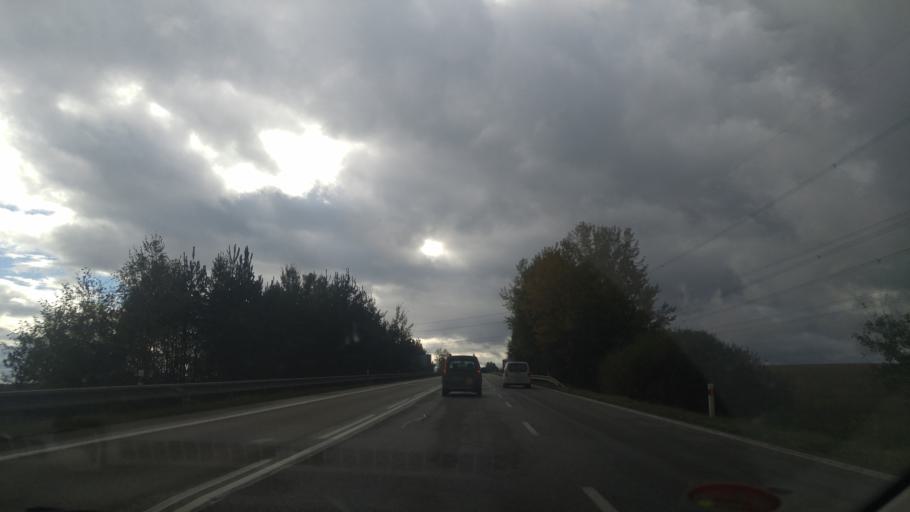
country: CZ
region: Jihocesky
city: Sevetin
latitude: 49.0715
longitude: 14.5374
